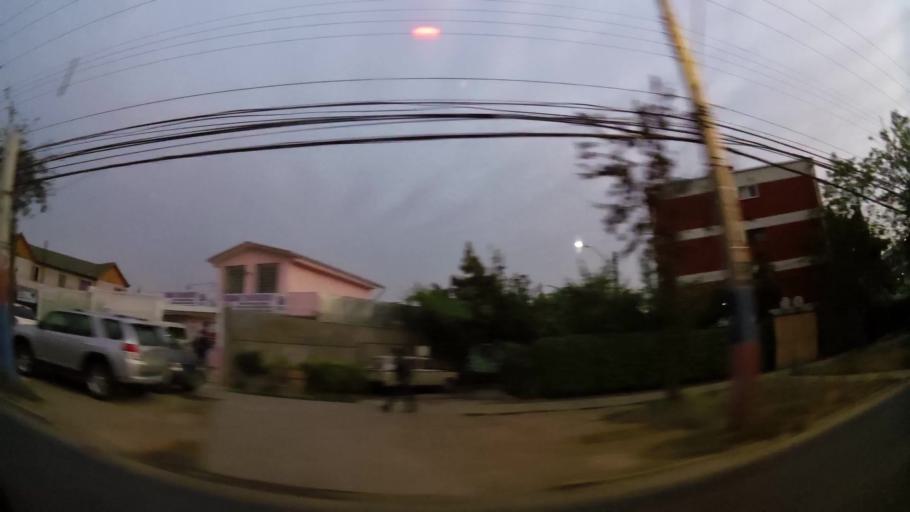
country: CL
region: Santiago Metropolitan
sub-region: Provincia de Santiago
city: Lo Prado
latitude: -33.4678
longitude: -70.7118
